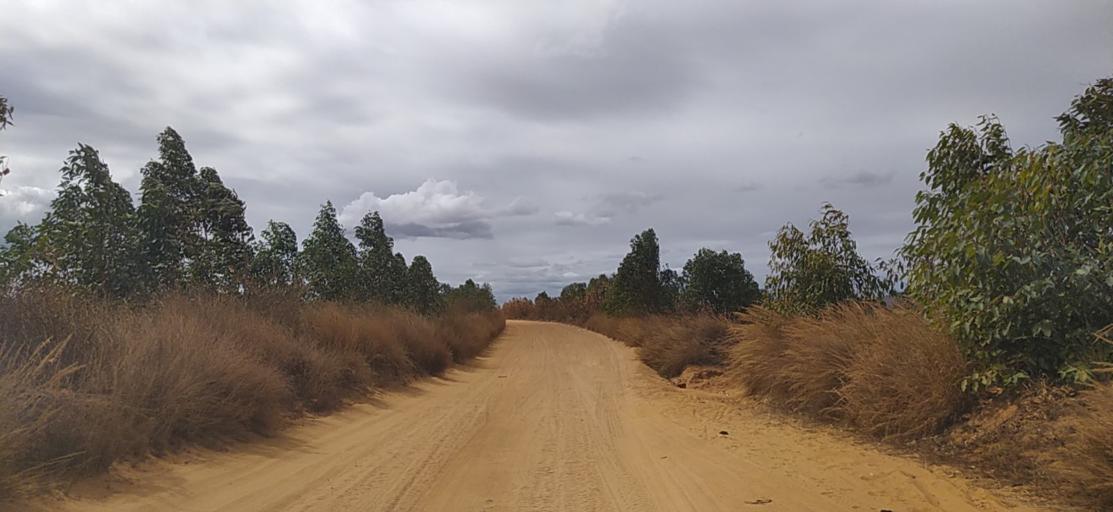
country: MG
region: Alaotra Mangoro
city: Ambatondrazaka
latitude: -17.9447
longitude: 48.2486
